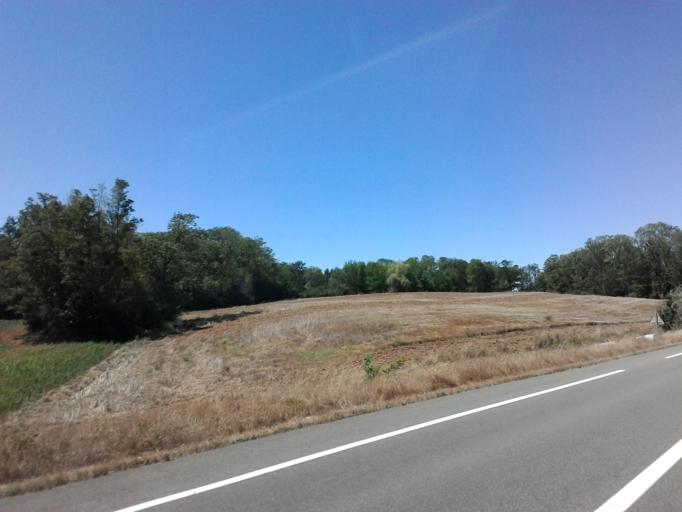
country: FR
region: Franche-Comte
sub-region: Departement du Jura
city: Montmorot
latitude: 46.6536
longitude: 5.5087
